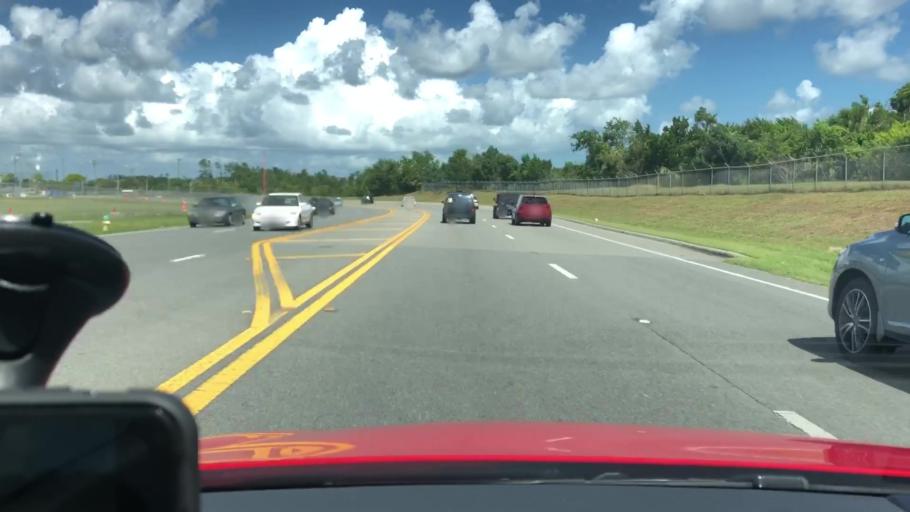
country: US
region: Florida
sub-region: Volusia County
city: Daytona Beach
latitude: 29.1852
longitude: -81.0436
